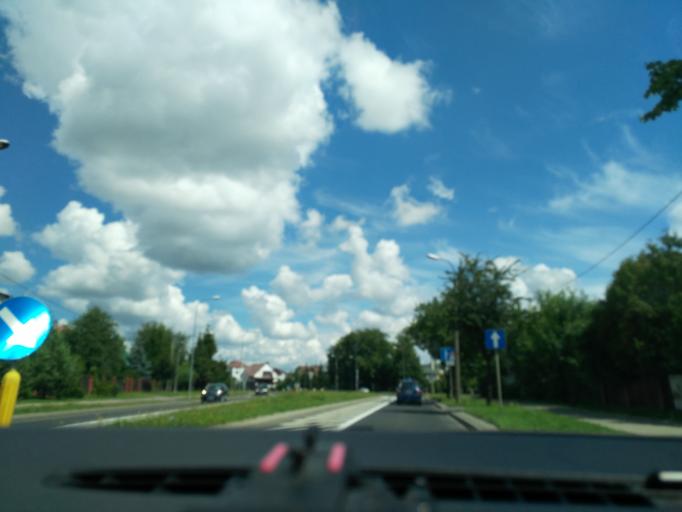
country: PL
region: Podlasie
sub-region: Powiat bielski
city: Bielsk Podlaski
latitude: 52.7773
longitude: 23.1874
